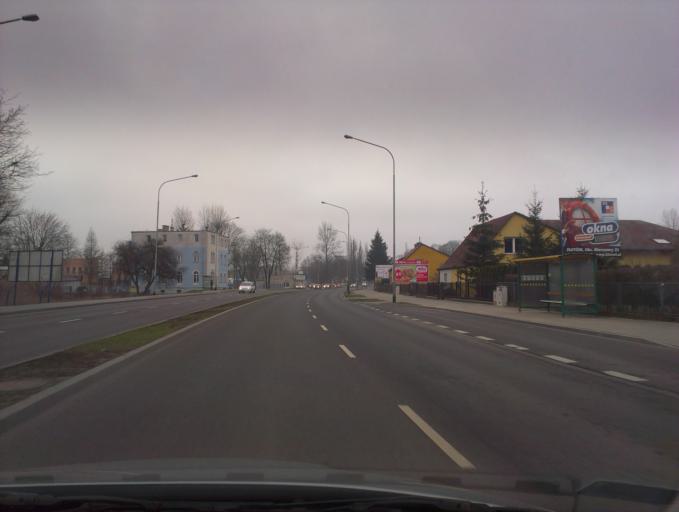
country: PL
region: Greater Poland Voivodeship
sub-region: Powiat pilski
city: Pila
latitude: 53.1407
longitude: 16.7490
